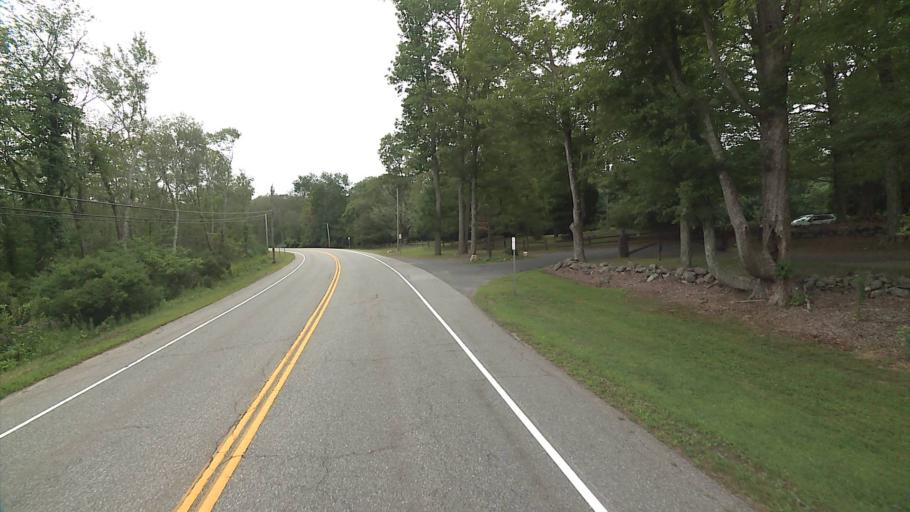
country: US
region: Connecticut
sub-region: Hartford County
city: Terramuggus
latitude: 41.7201
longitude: -72.4364
